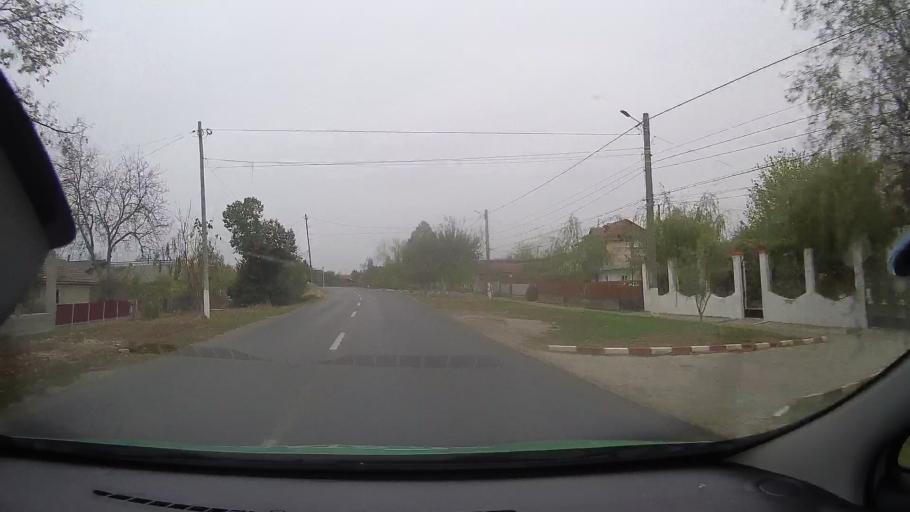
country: RO
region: Ialomita
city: Tandarei
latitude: 44.6526
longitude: 27.6548
